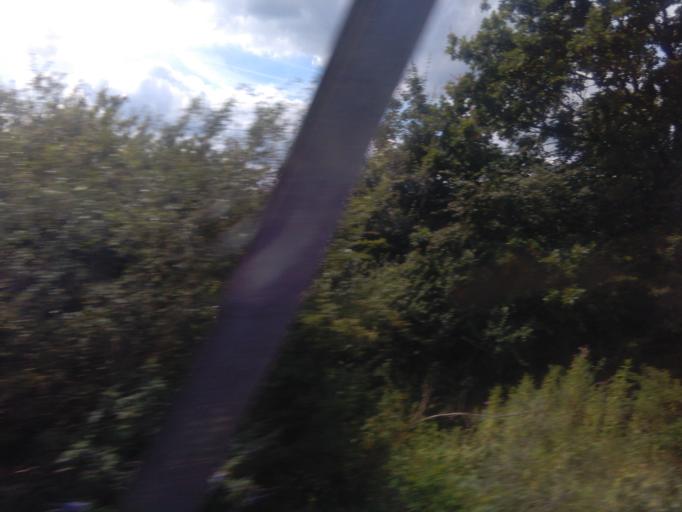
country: GB
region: England
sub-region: Hertfordshire
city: Borehamwood
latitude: 51.6622
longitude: -0.2905
